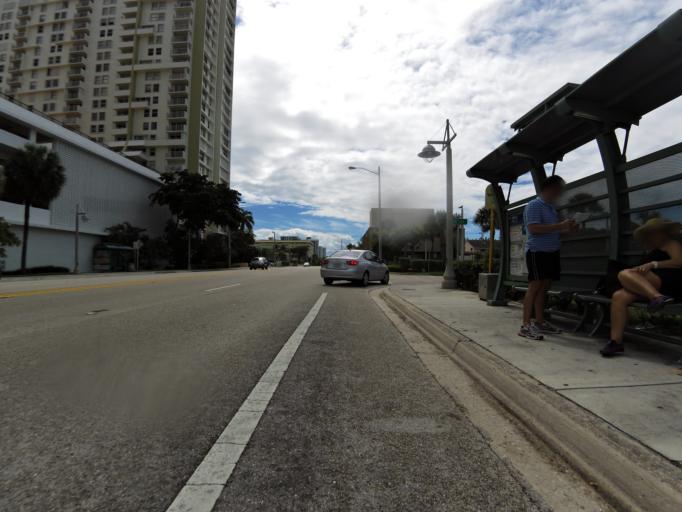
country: US
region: Florida
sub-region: Broward County
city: Terra Mar
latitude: 26.2312
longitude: -80.0910
